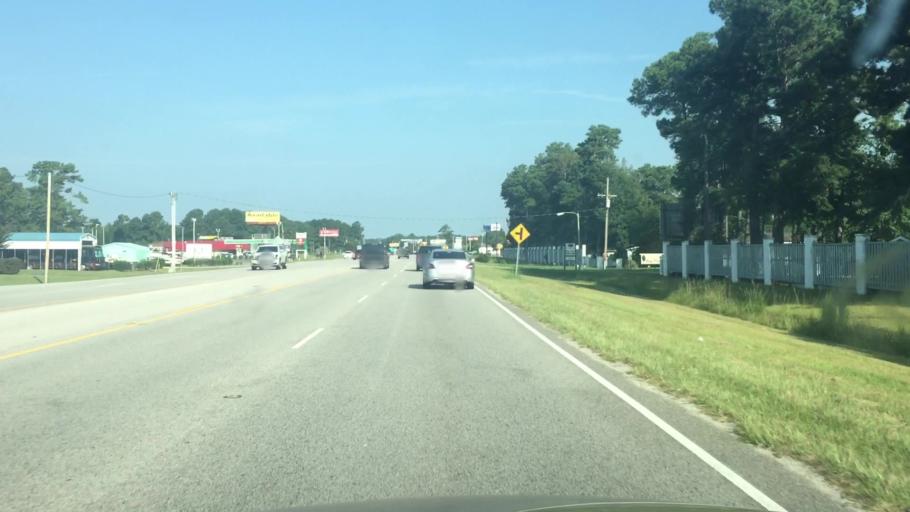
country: US
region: South Carolina
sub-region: Horry County
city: Little River
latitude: 33.8697
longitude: -78.6687
